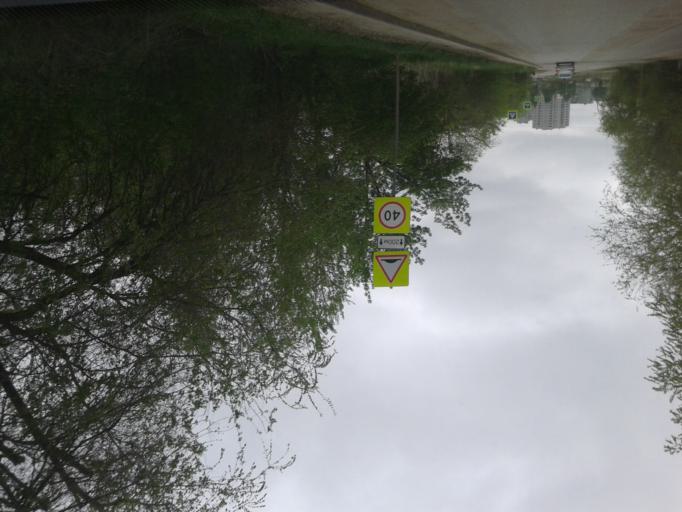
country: RU
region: Volgograd
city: Gorodishche
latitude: 48.7656
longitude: 44.4976
